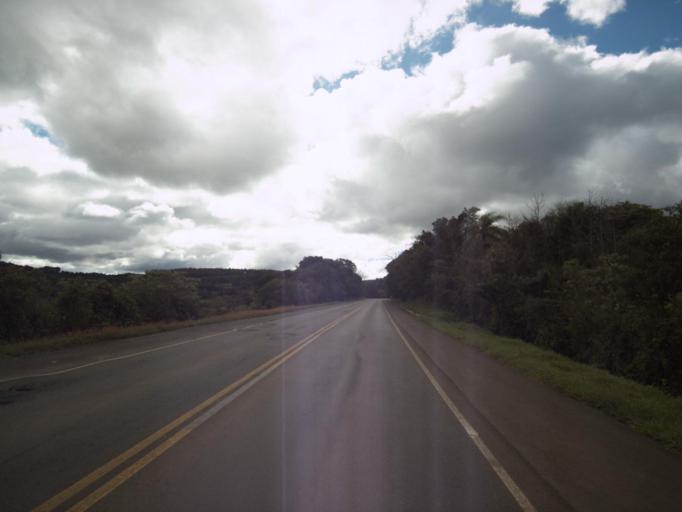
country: BR
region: Santa Catarina
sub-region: Concordia
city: Concordia
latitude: -27.2794
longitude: -51.9692
